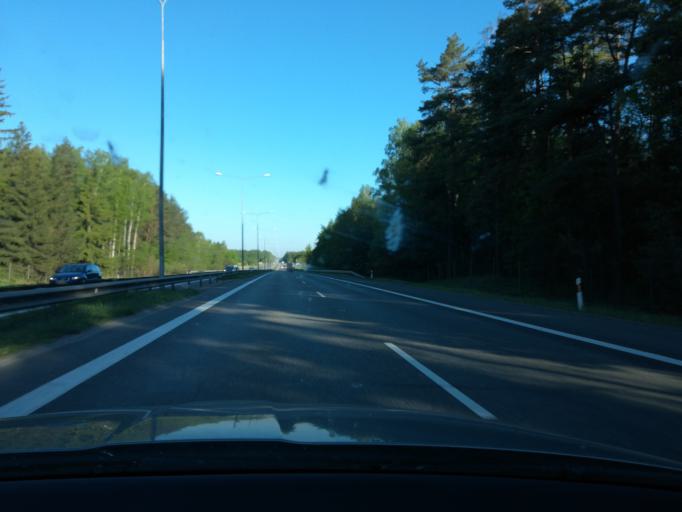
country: LT
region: Kauno apskritis
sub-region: Kauno rajonas
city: Karmelava
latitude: 54.8943
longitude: 24.1545
